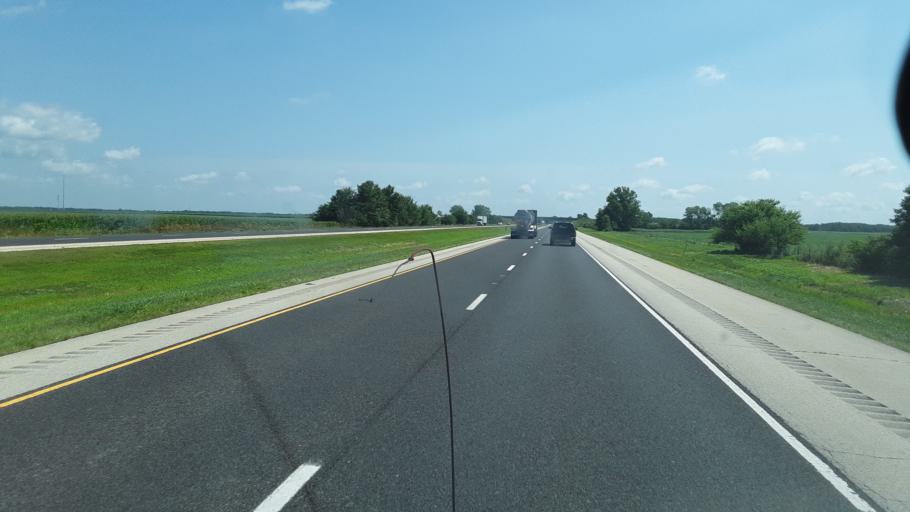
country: US
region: Illinois
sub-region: Clark County
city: Martinsville
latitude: 39.3766
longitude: -87.8425
